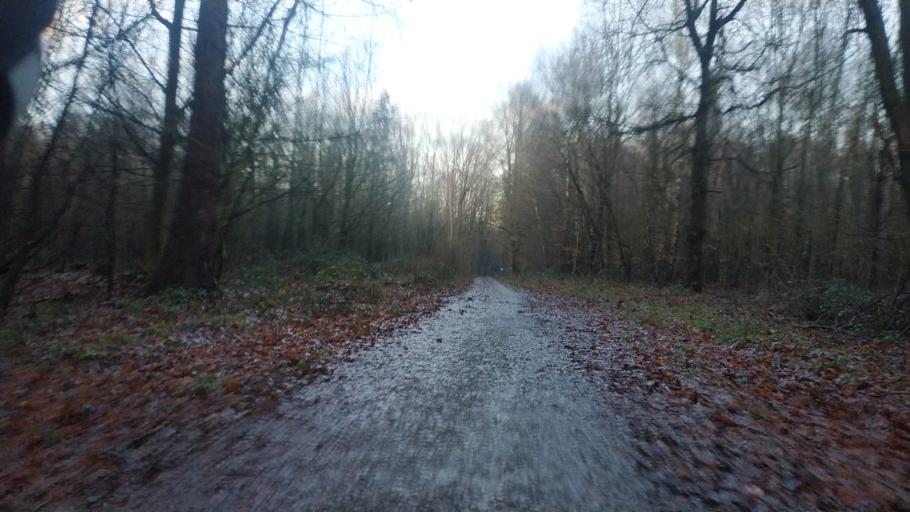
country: DE
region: North Rhine-Westphalia
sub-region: Regierungsbezirk Munster
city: Mettingen
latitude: 52.2857
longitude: 7.7820
